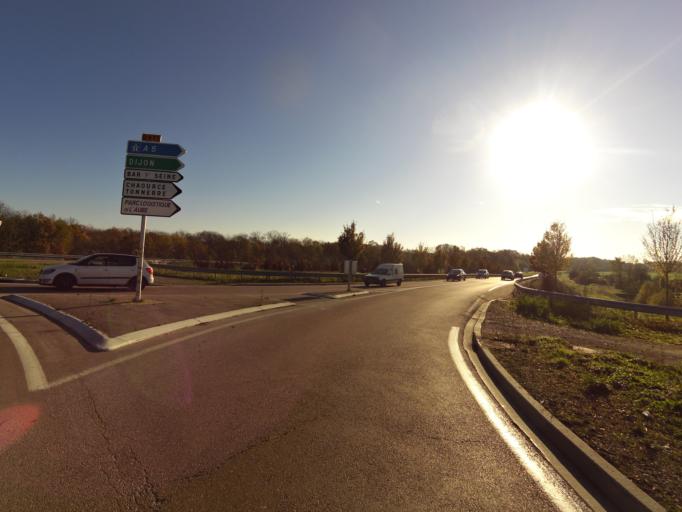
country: FR
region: Champagne-Ardenne
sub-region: Departement de l'Aube
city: Bucheres
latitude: 48.2504
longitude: 4.1122
